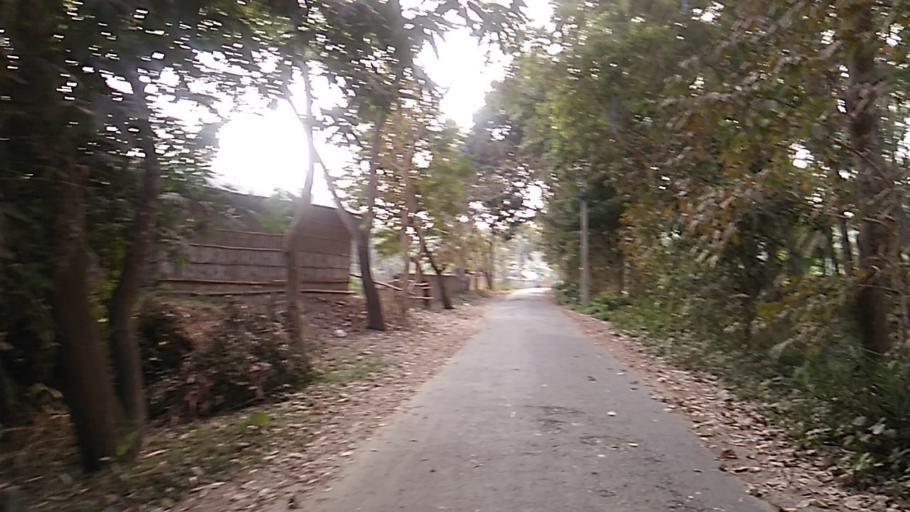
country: IN
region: West Bengal
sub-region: Nadia
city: Navadwip
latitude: 23.4271
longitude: 88.4001
